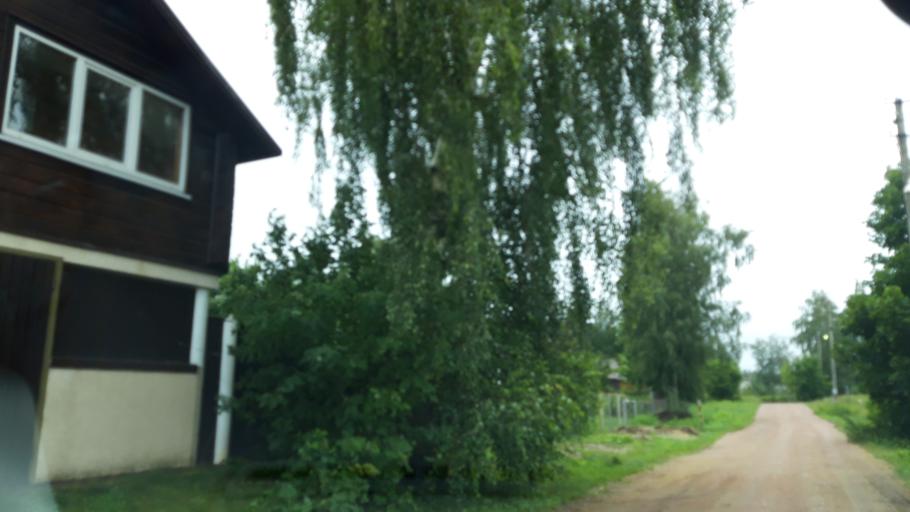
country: RU
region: Tverskaya
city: Konakovo
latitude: 56.6613
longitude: 36.6550
